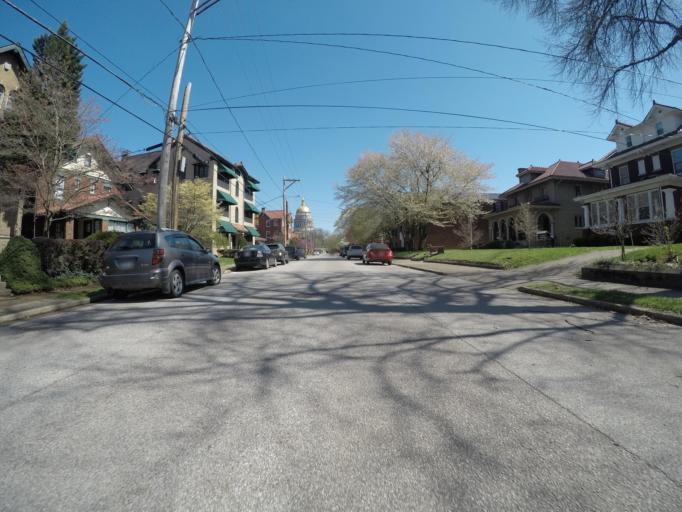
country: US
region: West Virginia
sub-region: Kanawha County
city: Charleston
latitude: 38.3380
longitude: -81.6170
